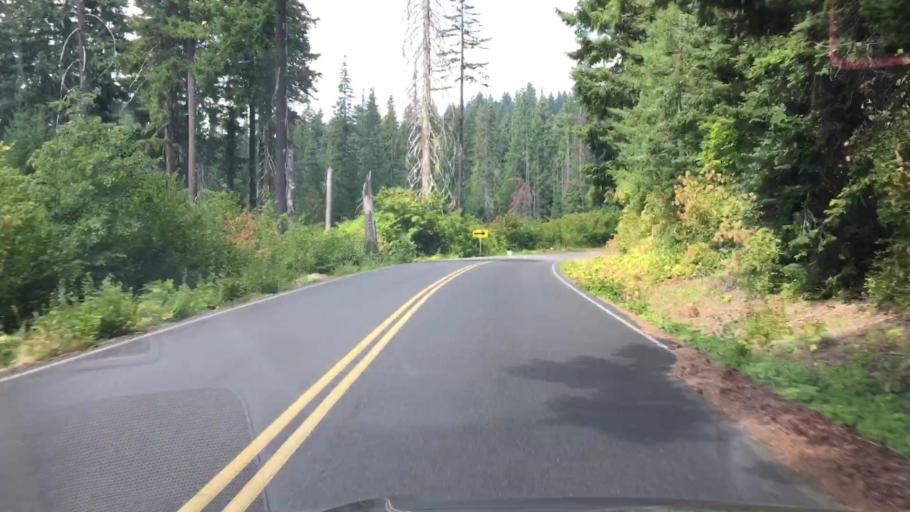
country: US
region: Washington
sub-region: Klickitat County
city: White Salmon
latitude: 46.0448
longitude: -121.5562
